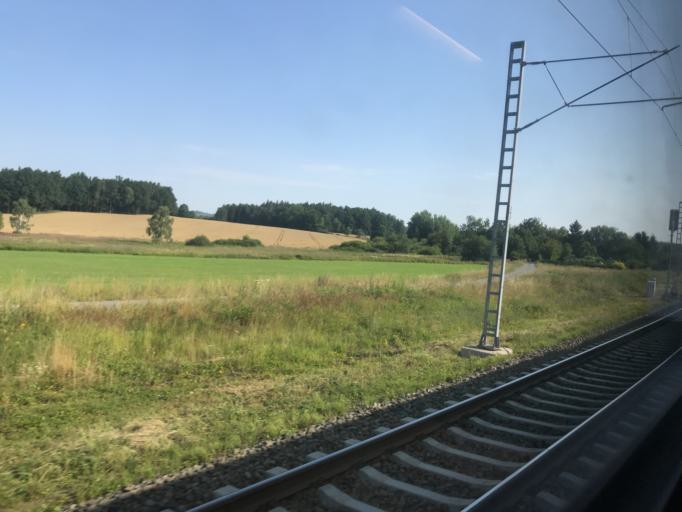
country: CZ
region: Jihocesky
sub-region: Okres Tabor
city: Tabor
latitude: 49.4328
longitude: 14.6833
